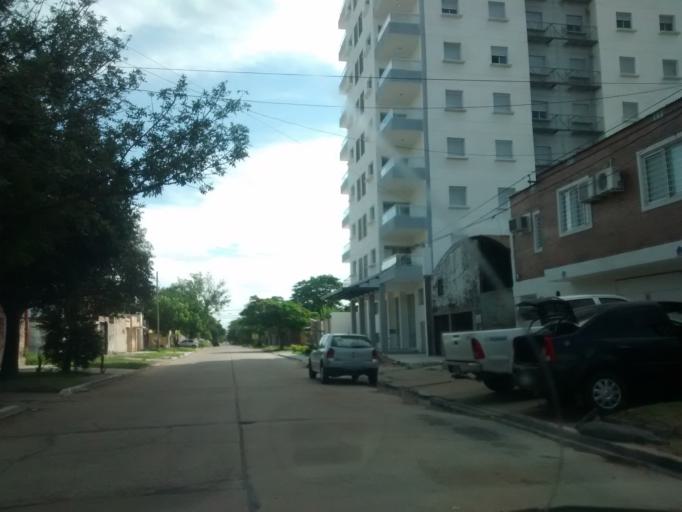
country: AR
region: Chaco
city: Resistencia
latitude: -27.4403
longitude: -58.9904
